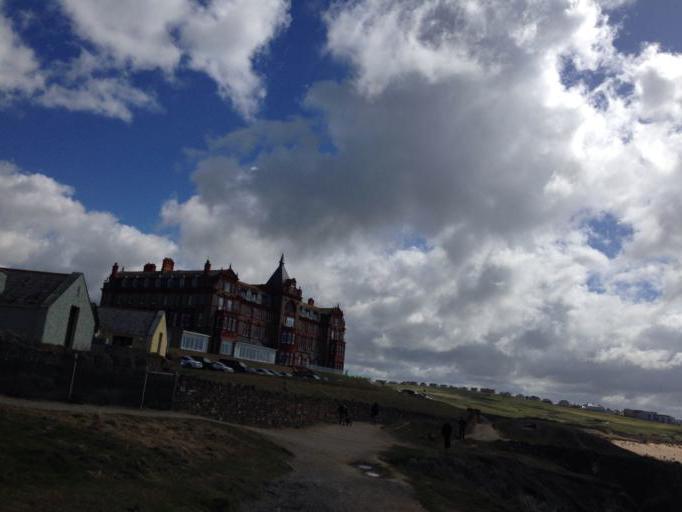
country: GB
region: England
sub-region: Cornwall
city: Newquay
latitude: 50.4217
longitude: -5.0980
